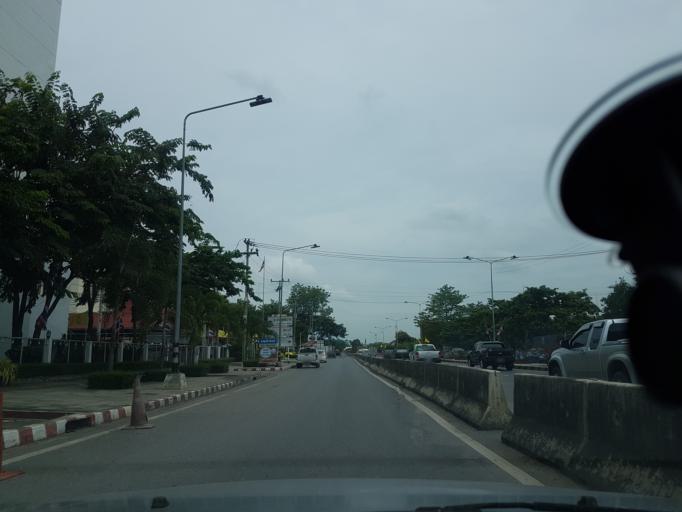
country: TH
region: Lop Buri
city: Lop Buri
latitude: 14.8024
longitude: 100.6525
